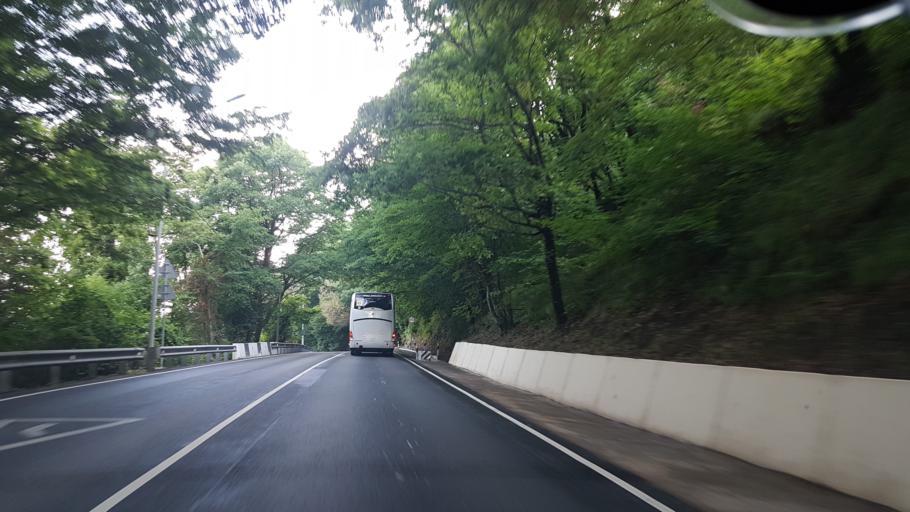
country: RU
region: Krasnodarskiy
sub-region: Sochi City
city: Lazarevskoye
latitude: 43.8431
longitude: 39.4137
